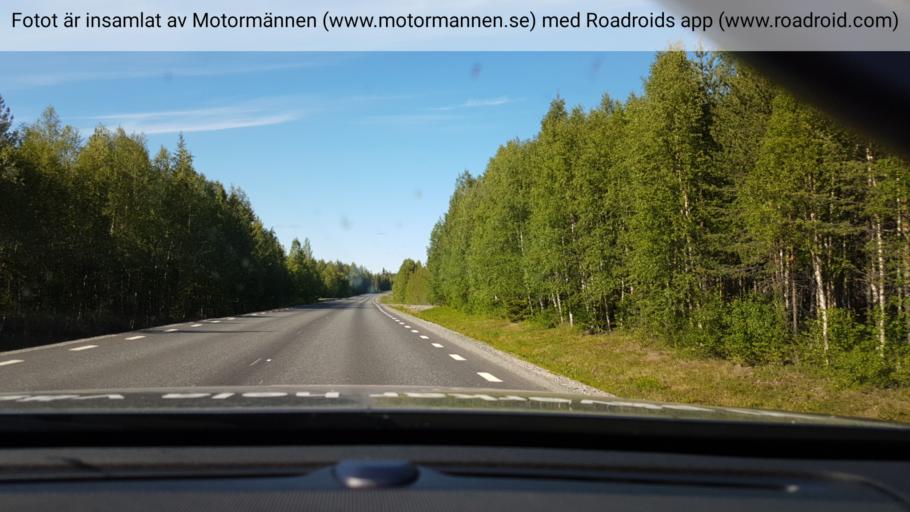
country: SE
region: Vaesterbotten
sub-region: Lycksele Kommun
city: Lycksele
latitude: 64.7992
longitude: 18.7317
